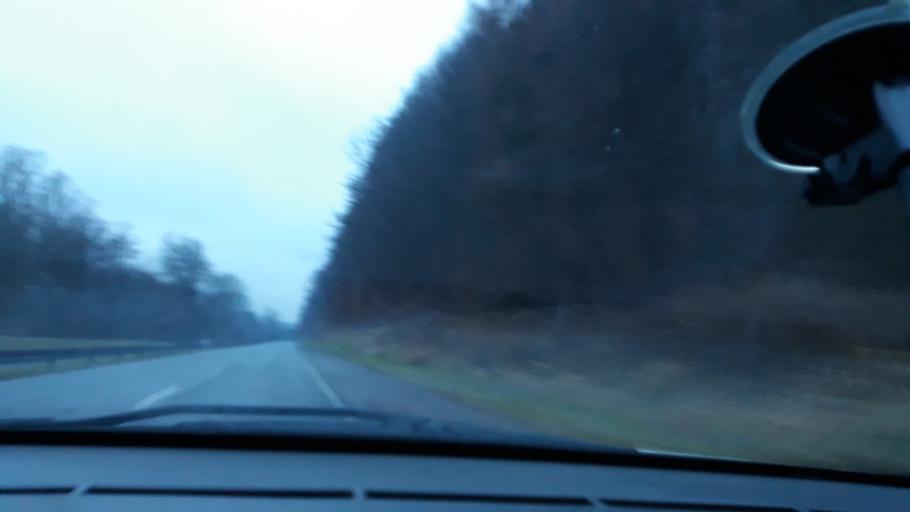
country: DE
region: Saarland
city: Blieskastel
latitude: 49.2254
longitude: 7.2591
